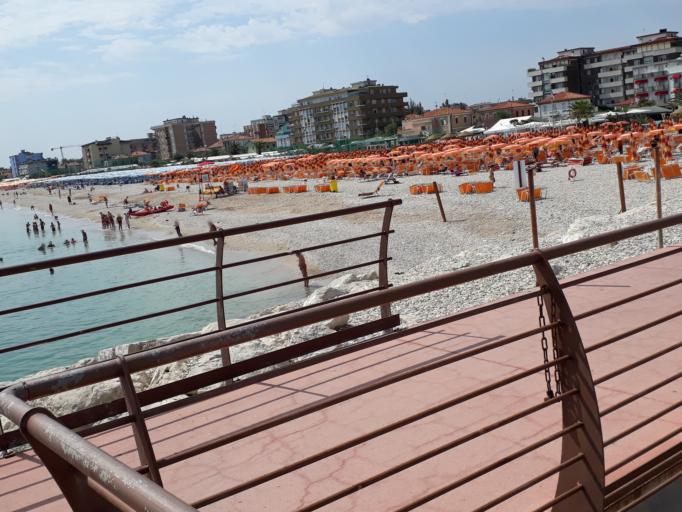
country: IT
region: The Marches
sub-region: Provincia di Pesaro e Urbino
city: Fano
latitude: 43.8499
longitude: 13.0219
